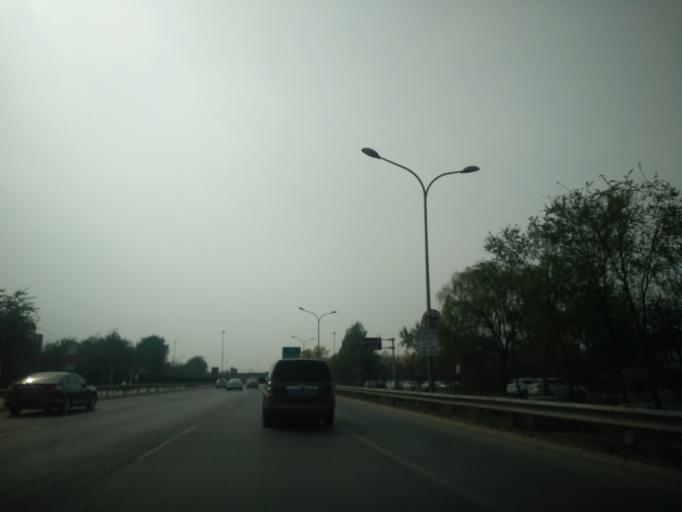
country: CN
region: Beijing
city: Dongfeng
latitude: 39.8677
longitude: 116.5504
